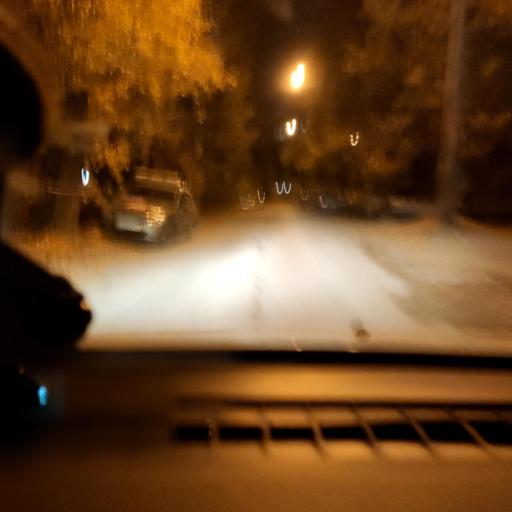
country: RU
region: Samara
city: Samara
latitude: 53.2183
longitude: 50.1602
